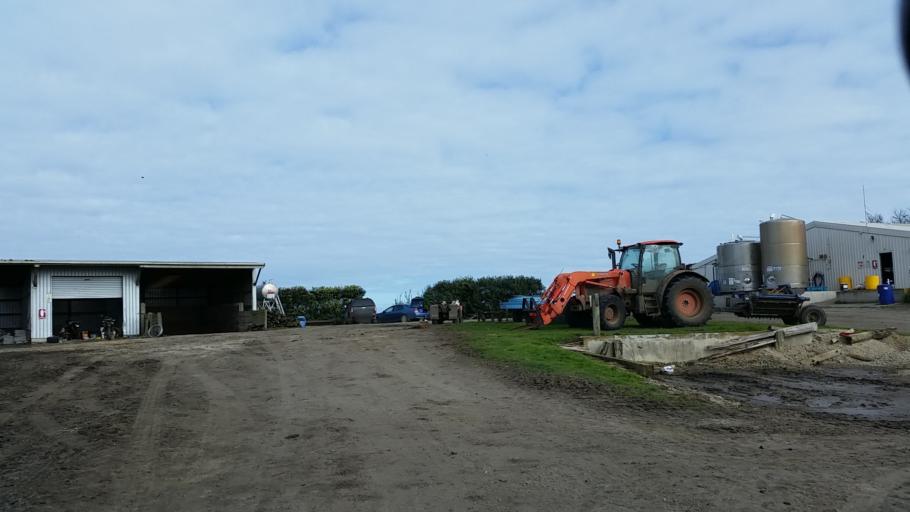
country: NZ
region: Taranaki
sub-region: South Taranaki District
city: Patea
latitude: -39.8245
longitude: 174.6494
